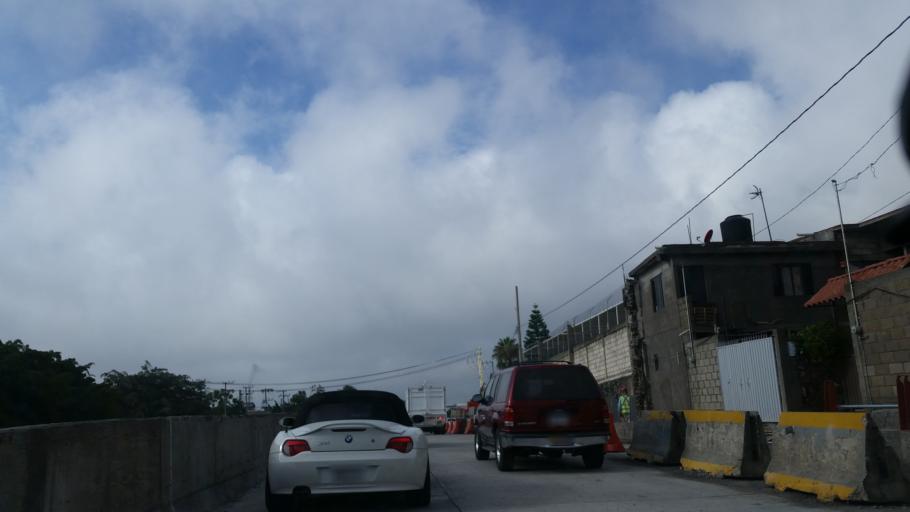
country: MX
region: Morelos
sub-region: Cuernavaca
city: Colonia los Cerritos
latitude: 18.9413
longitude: -99.1901
